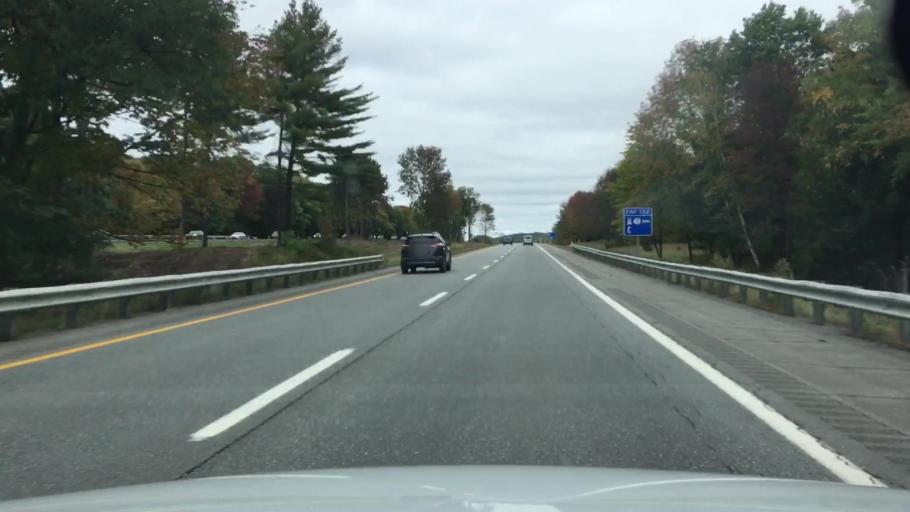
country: US
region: Maine
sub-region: Somerset County
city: Fairfield
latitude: 44.5848
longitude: -69.6233
